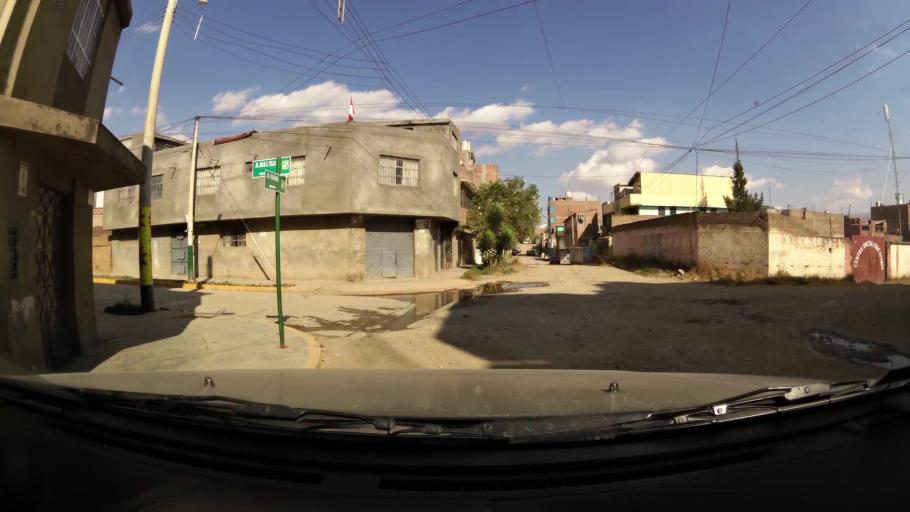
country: PE
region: Junin
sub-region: Provincia de Huancayo
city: El Tambo
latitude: -12.0631
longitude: -75.2210
